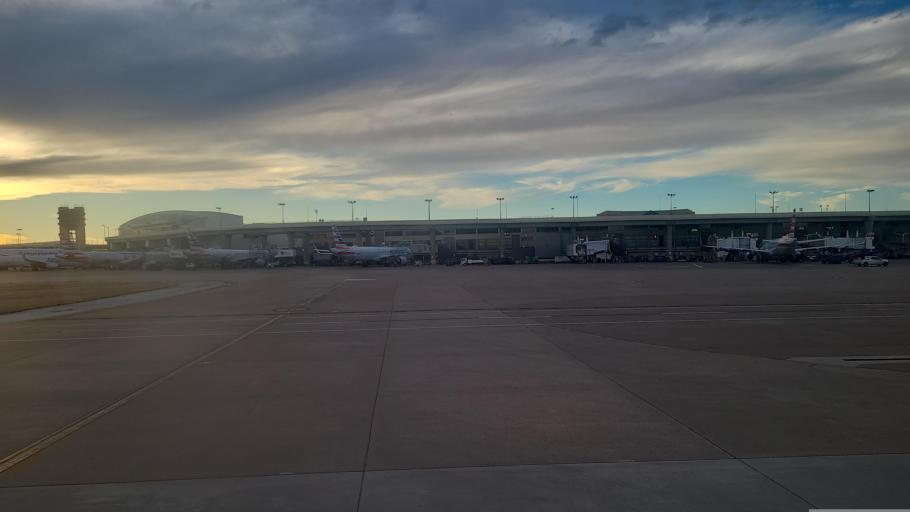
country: US
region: Texas
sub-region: Dallas County
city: Coppell
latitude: 32.9034
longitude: -97.0331
